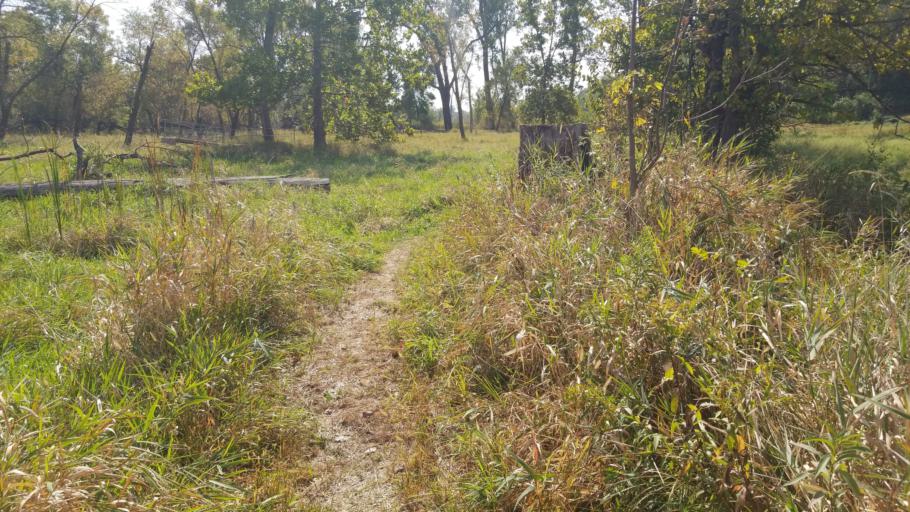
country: US
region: Nebraska
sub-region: Sarpy County
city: Bellevue
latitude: 41.1720
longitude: -95.8909
